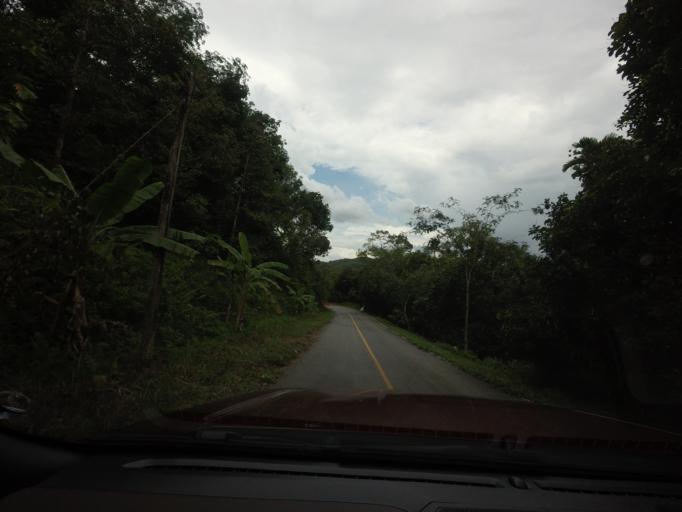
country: TH
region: Narathiwat
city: Sukhirin
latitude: 5.9999
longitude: 101.6976
